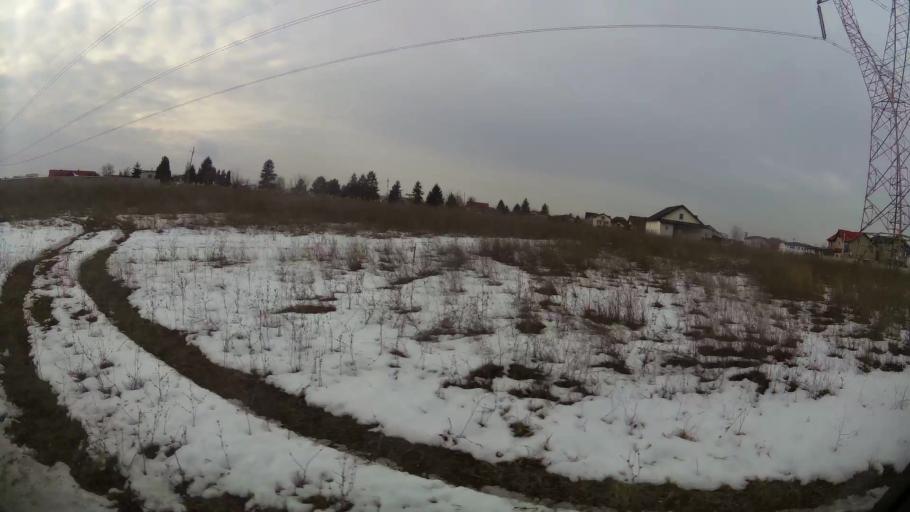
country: RO
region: Ilfov
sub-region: Comuna Glina
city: Catelu
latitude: 44.4027
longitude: 26.2261
